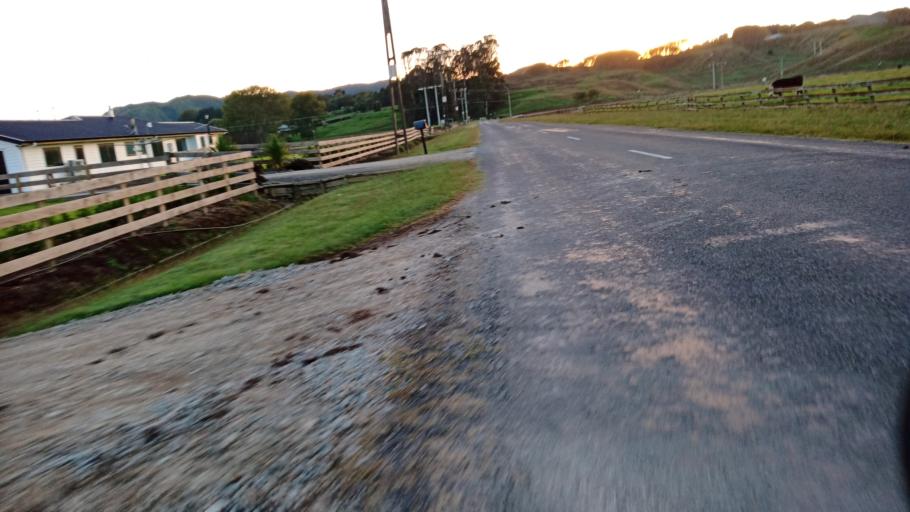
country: NZ
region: Gisborne
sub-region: Gisborne District
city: Gisborne
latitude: -38.6327
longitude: 177.9894
